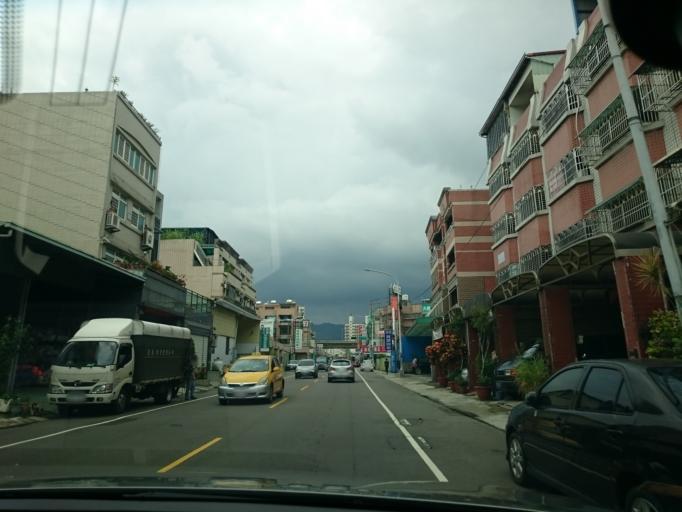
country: TW
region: Taiwan
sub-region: Taichung City
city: Taichung
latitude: 24.1406
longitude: 120.7070
